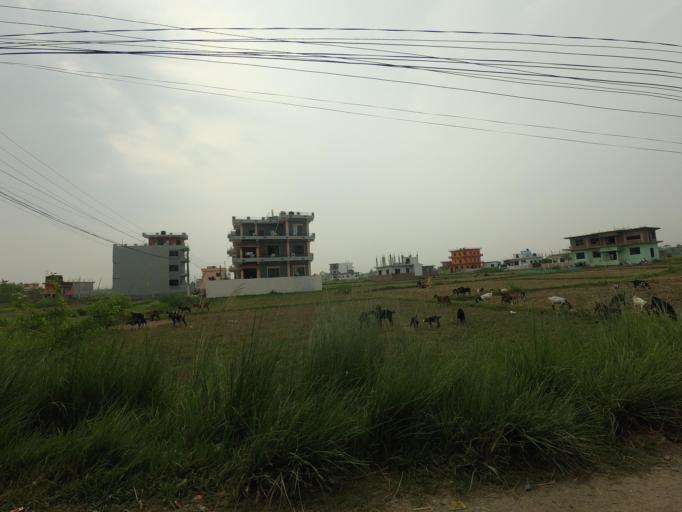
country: NP
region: Western Region
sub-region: Lumbini Zone
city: Bhairahawa
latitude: 27.4881
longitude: 83.4493
